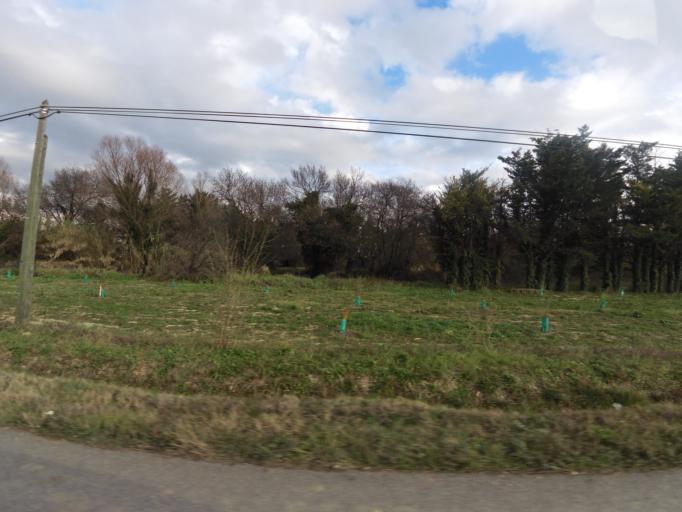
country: FR
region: Languedoc-Roussillon
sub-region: Departement du Gard
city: Calvisson
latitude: 43.7732
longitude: 4.1988
